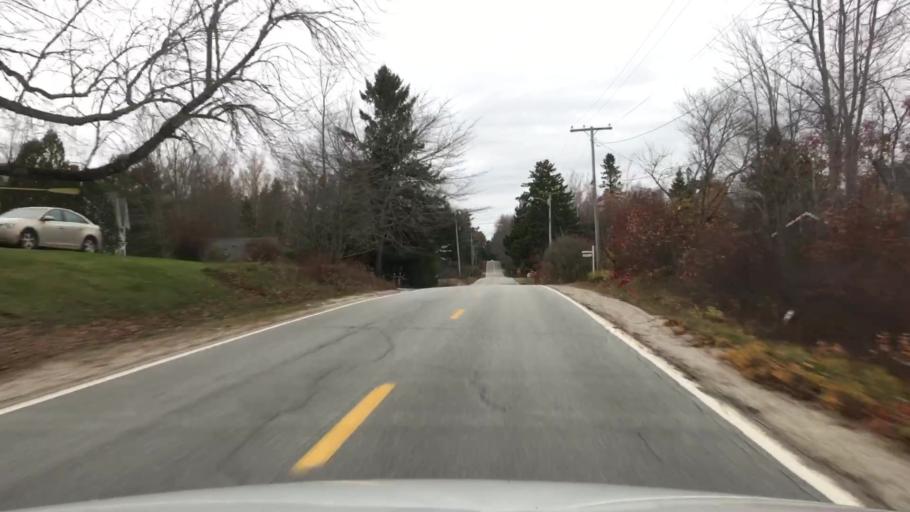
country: US
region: Maine
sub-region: Hancock County
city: Sedgwick
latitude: 44.3152
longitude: -68.5705
